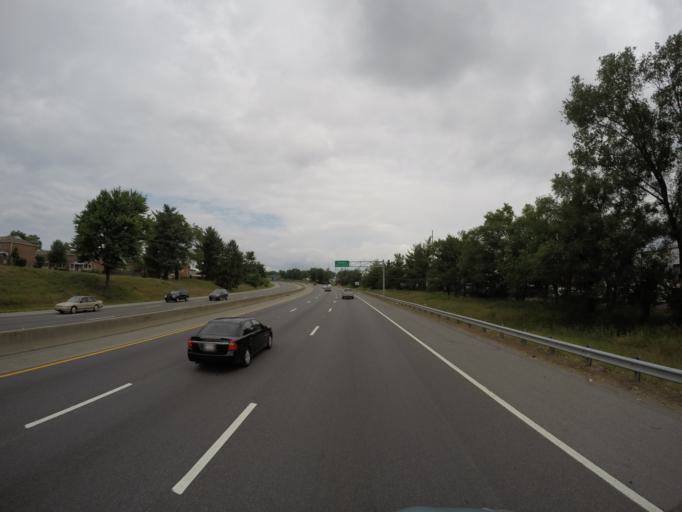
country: US
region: Virginia
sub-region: City of Roanoke
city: Roanoke
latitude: 37.2865
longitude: -79.9387
